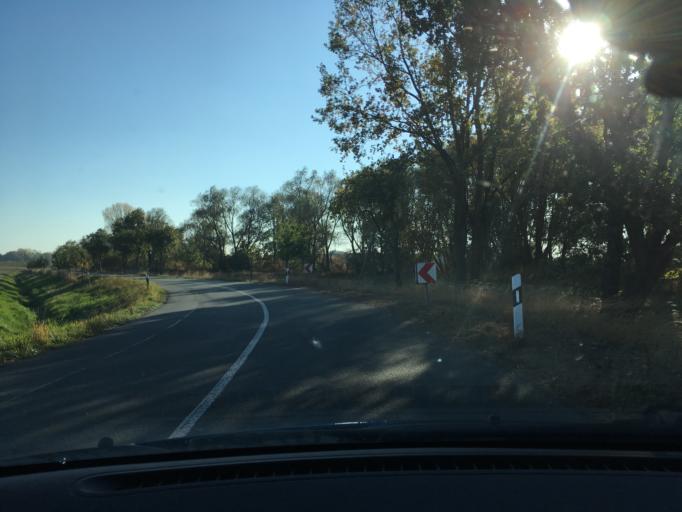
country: DE
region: Lower Saxony
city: Damnatz
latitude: 53.1697
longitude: 11.1265
